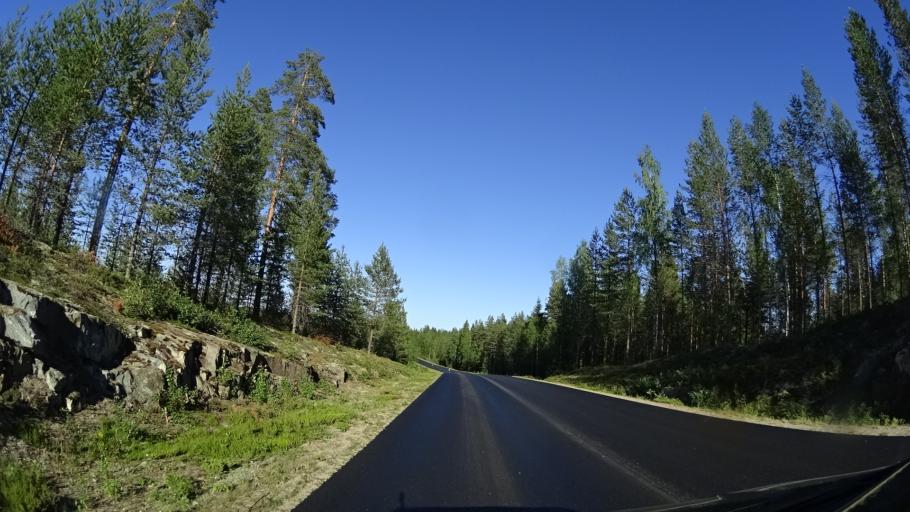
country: FI
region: North Karelia
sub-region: Pielisen Karjala
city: Valtimo
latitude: 63.5602
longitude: 28.5992
